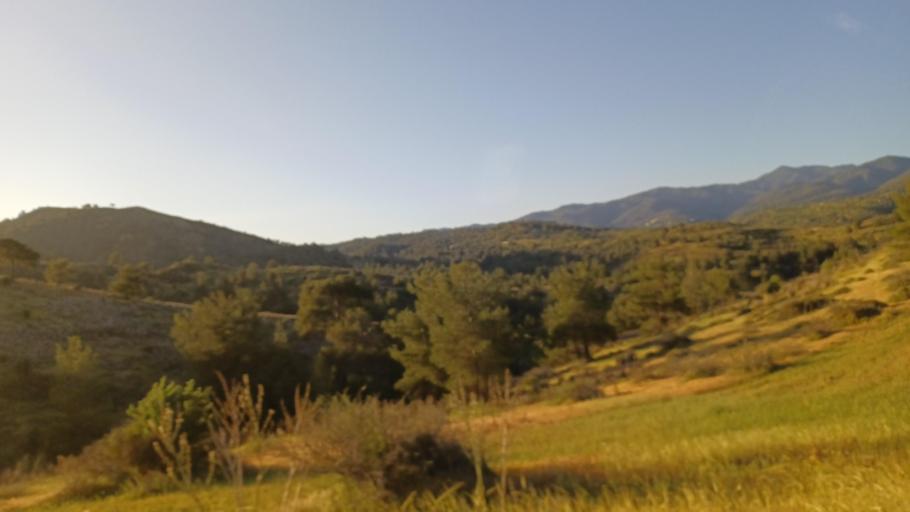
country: CY
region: Lefkosia
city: Astromeritis
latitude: 35.0642
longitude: 33.0311
